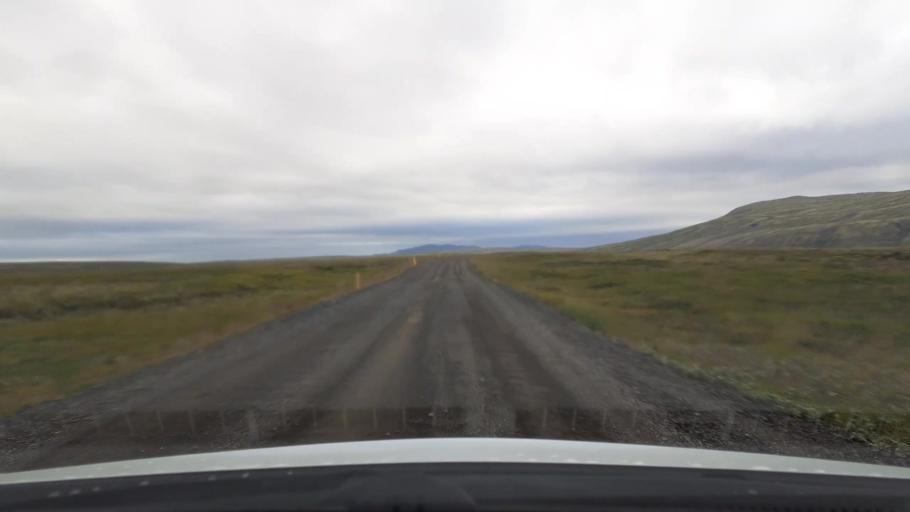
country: IS
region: Capital Region
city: Mosfellsbaer
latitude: 64.1942
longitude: -21.5447
